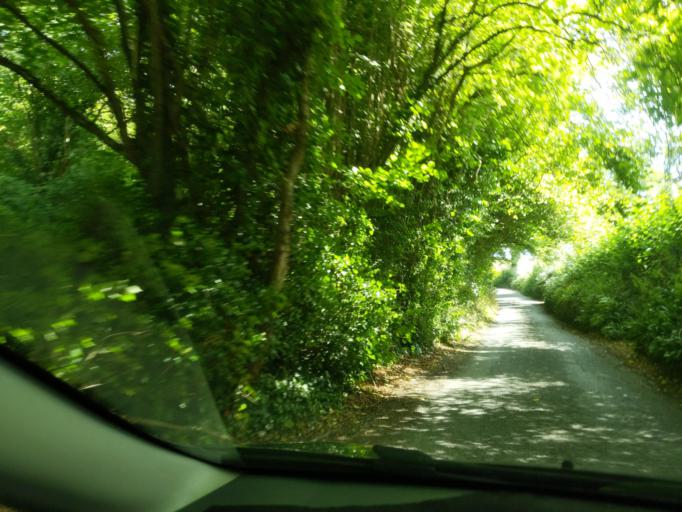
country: GB
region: England
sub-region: Cornwall
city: Torpoint
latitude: 50.3566
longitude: -4.2242
